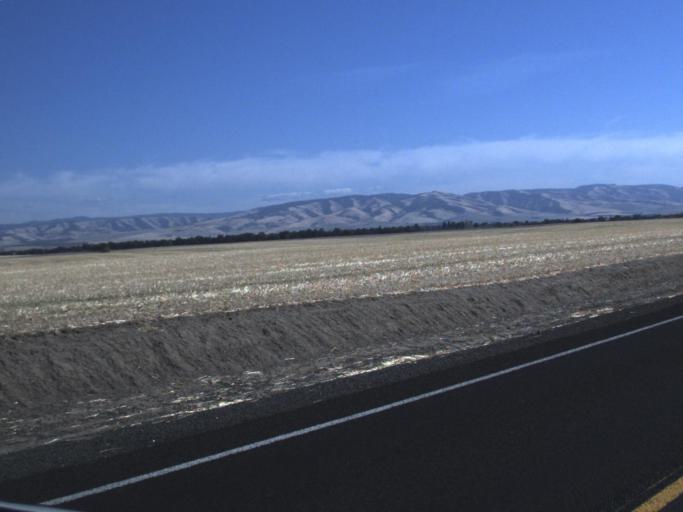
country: US
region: Washington
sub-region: Walla Walla County
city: Walla Walla
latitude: 46.0940
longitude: -118.3680
